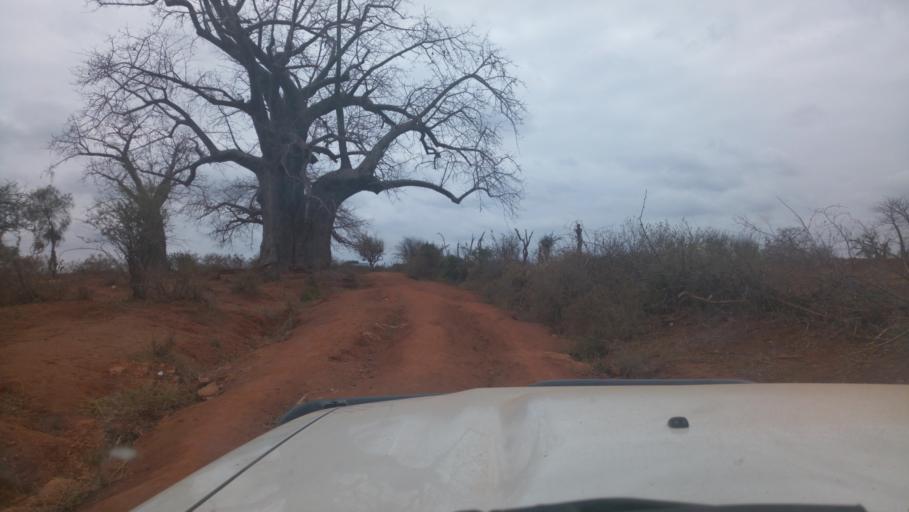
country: KE
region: Makueni
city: Makueni
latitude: -1.9672
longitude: 38.0798
